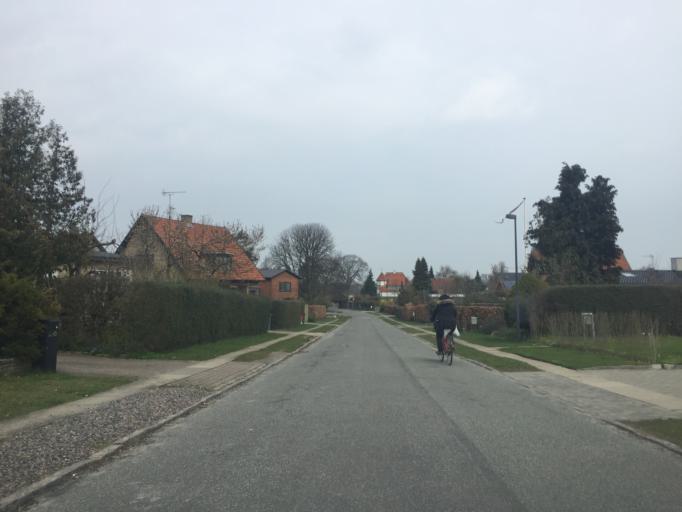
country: DK
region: Capital Region
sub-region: Kobenhavn
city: Vanlose
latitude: 55.7090
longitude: 12.4929
